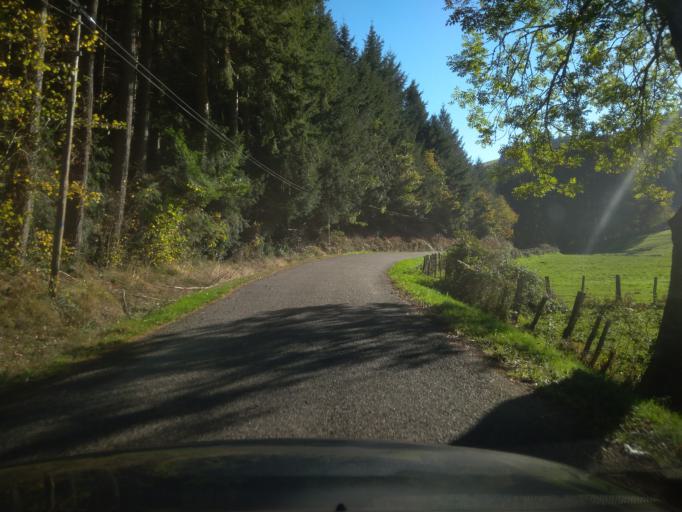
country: FR
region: Rhone-Alpes
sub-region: Departement de la Loire
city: Ambierle
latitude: 46.1291
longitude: 3.8521
